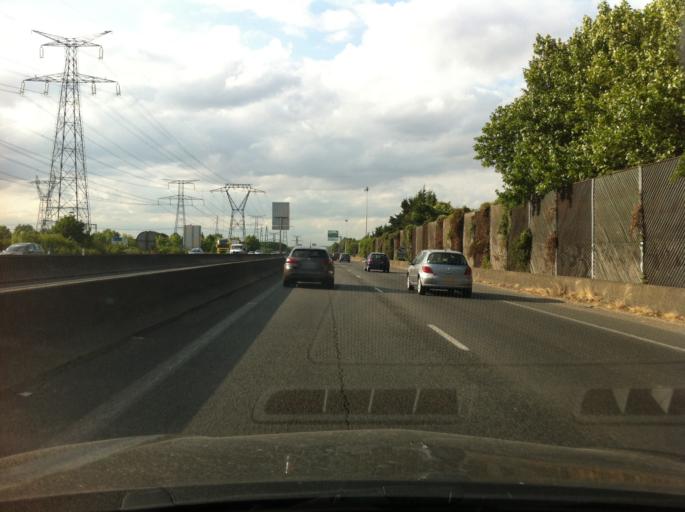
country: FR
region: Ile-de-France
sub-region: Departement de Seine-et-Marne
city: Collegien
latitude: 48.8386
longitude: 2.6645
